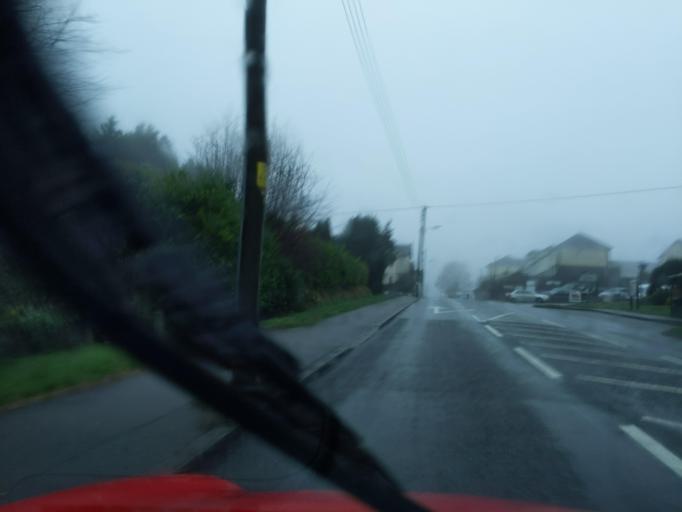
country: GB
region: England
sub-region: Cornwall
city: Callington
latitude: 50.5187
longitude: -4.3157
